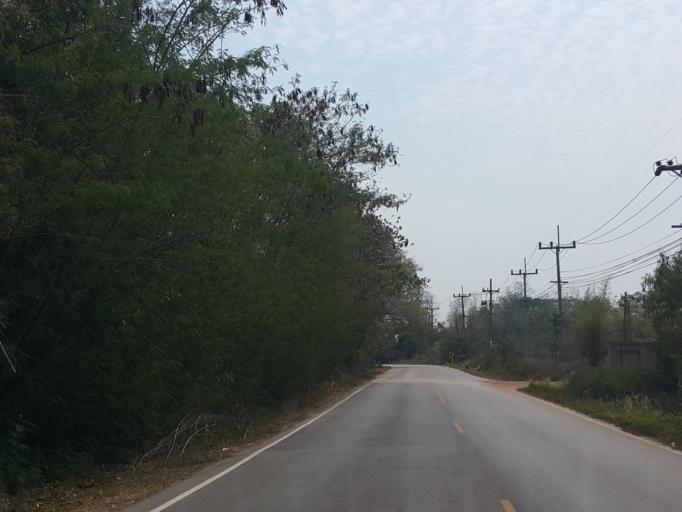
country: TH
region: Lampang
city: Chae Hom
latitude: 18.7628
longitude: 99.5554
